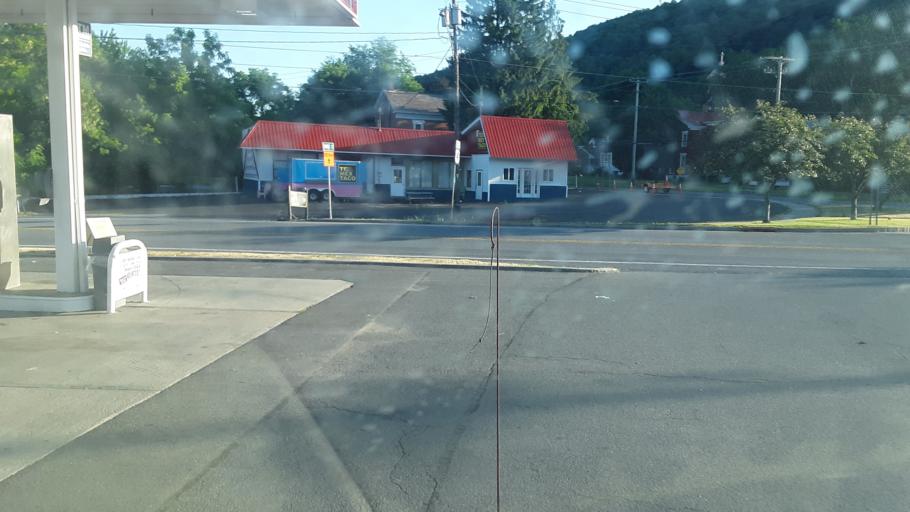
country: US
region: New York
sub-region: Washington County
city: Whitehall
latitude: 43.5500
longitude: -73.3976
